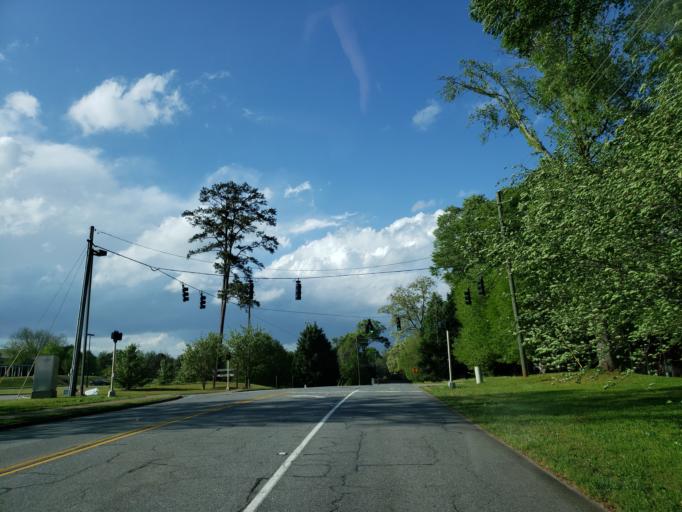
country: US
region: Georgia
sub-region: Fulton County
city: Alpharetta
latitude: 34.0586
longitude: -84.3347
